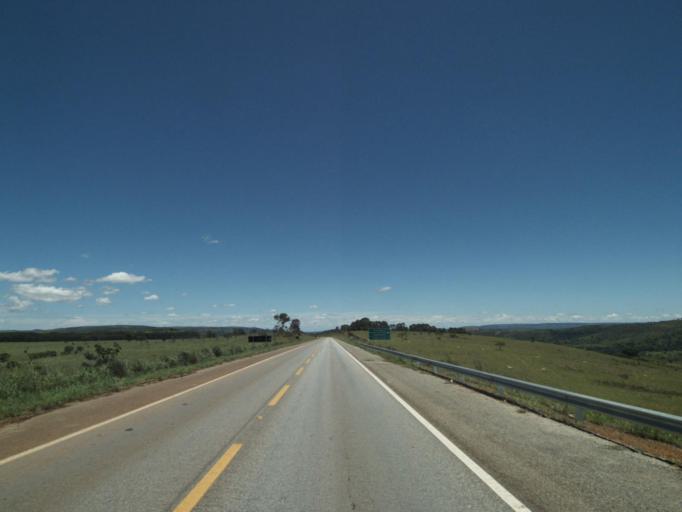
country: BR
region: Goias
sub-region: Pirenopolis
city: Pirenopolis
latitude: -15.7572
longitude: -48.7407
